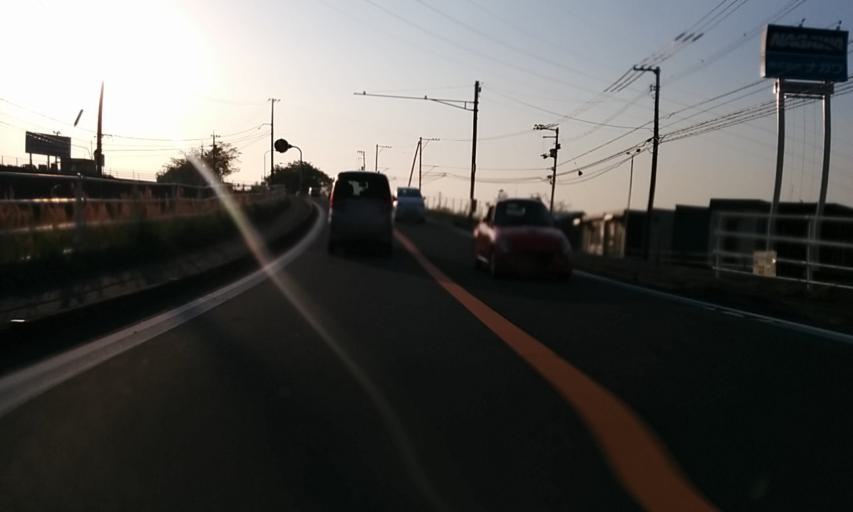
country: JP
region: Ehime
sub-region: Shikoku-chuo Shi
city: Matsuyama
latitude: 33.7885
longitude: 132.7803
